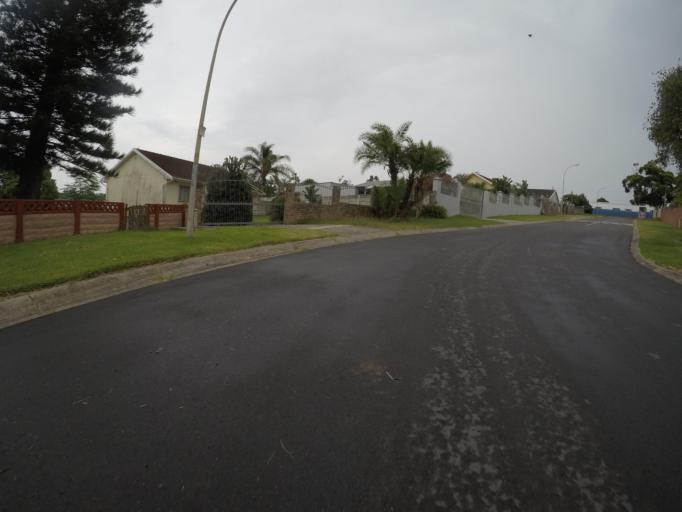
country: ZA
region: Eastern Cape
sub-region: Buffalo City Metropolitan Municipality
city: East London
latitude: -32.9885
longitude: 27.8560
